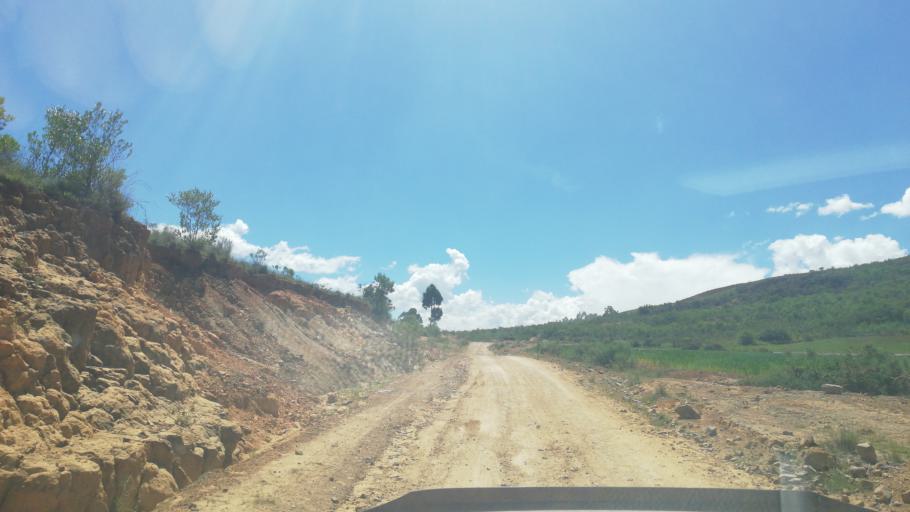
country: BO
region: Cochabamba
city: Totora
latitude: -17.7372
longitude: -65.2217
